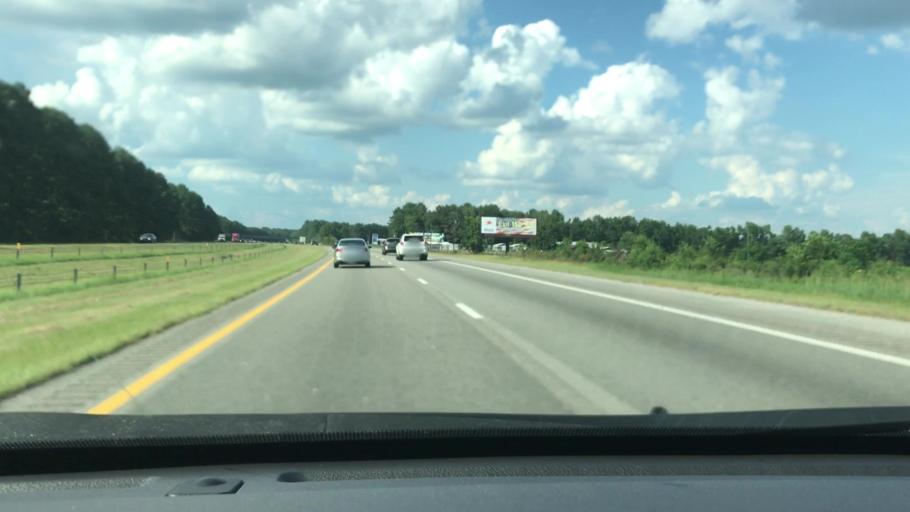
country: US
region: South Carolina
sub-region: Florence County
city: Timmonsville
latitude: 33.9608
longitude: -80.0453
